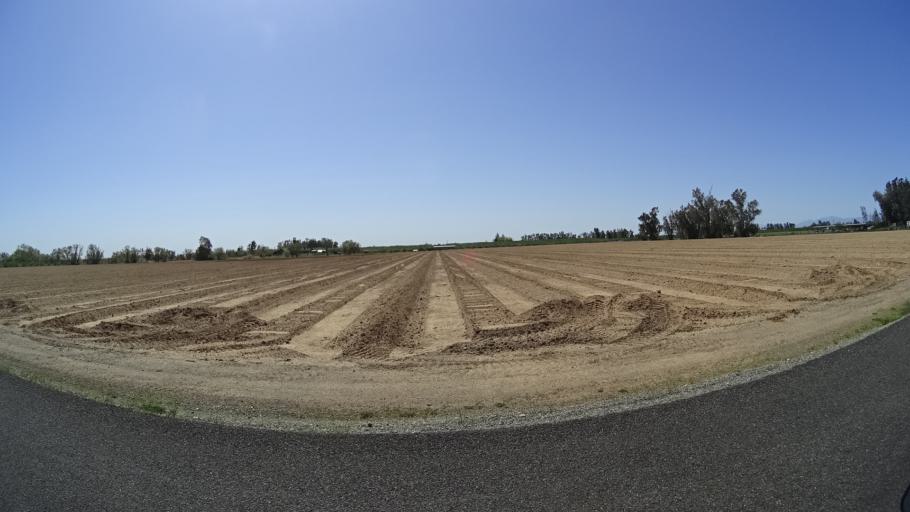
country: US
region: California
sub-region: Glenn County
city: Hamilton City
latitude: 39.7899
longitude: -122.0696
